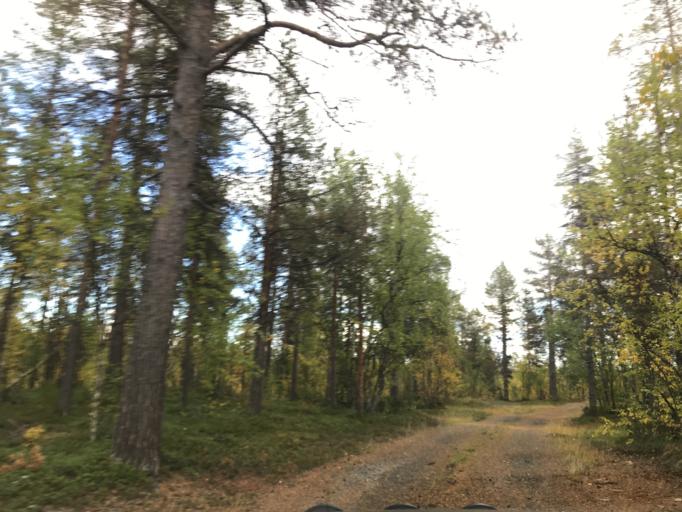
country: SE
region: Norrbotten
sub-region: Gallivare Kommun
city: Malmberget
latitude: 67.5849
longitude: 20.8516
